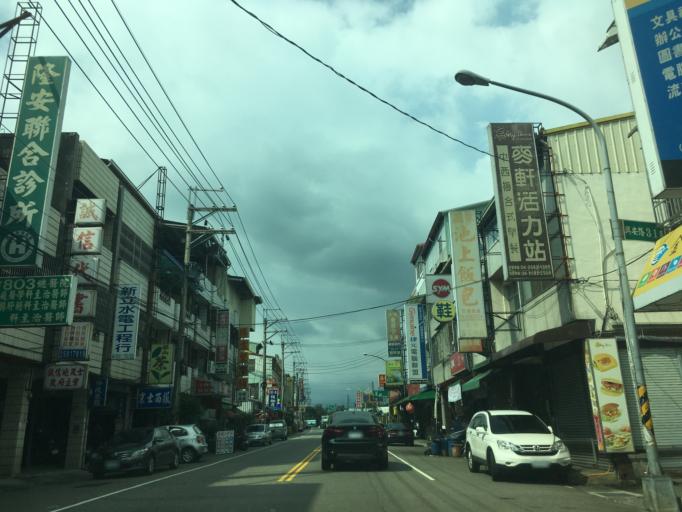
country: TW
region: Taiwan
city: Fengyuan
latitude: 24.2418
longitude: 120.8090
